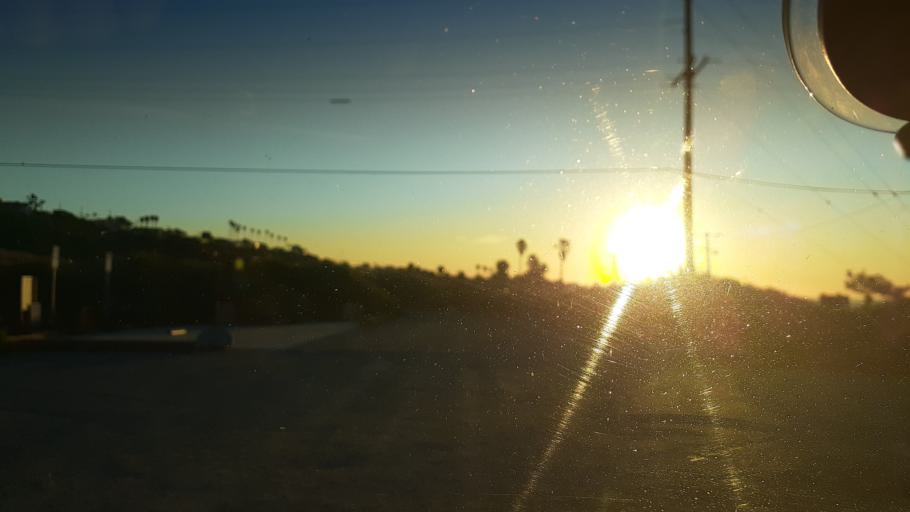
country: US
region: California
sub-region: Los Angeles County
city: San Pedro
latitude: 33.7160
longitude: -118.3150
